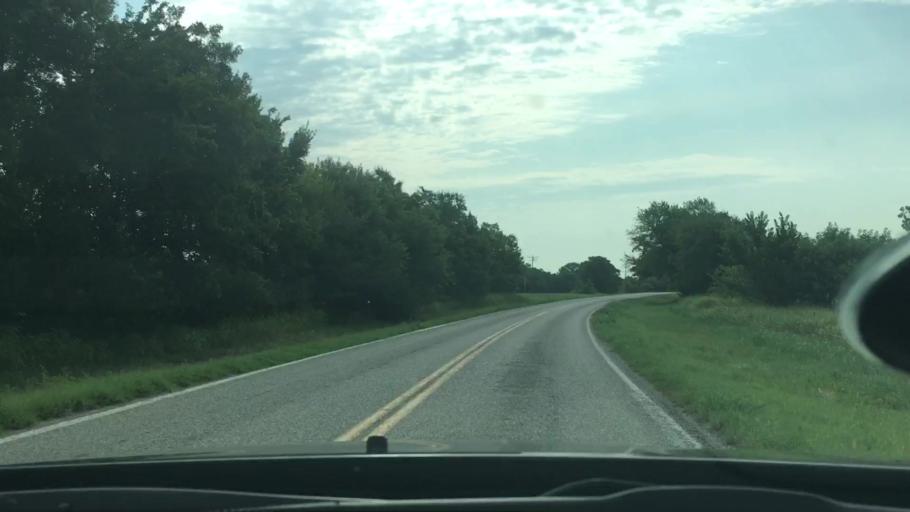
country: US
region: Oklahoma
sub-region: Johnston County
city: Tishomingo
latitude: 34.1656
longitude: -96.5729
